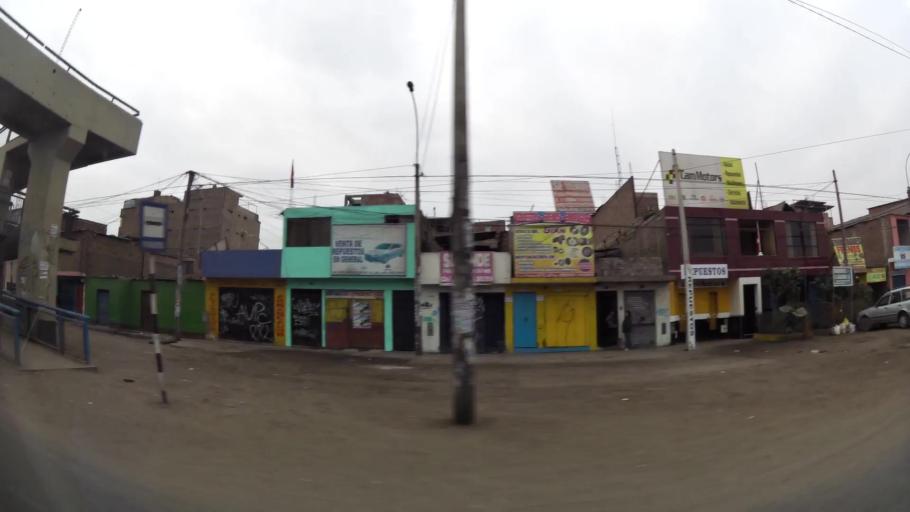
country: PE
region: Lima
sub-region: Lima
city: Surco
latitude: -12.1552
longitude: -76.9678
